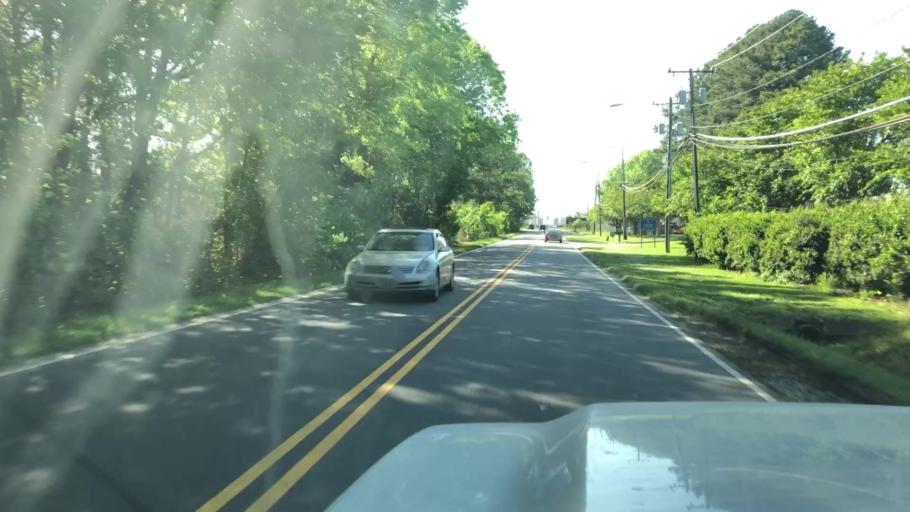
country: US
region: North Carolina
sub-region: Mecklenburg County
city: Charlotte
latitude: 35.2805
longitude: -80.9016
